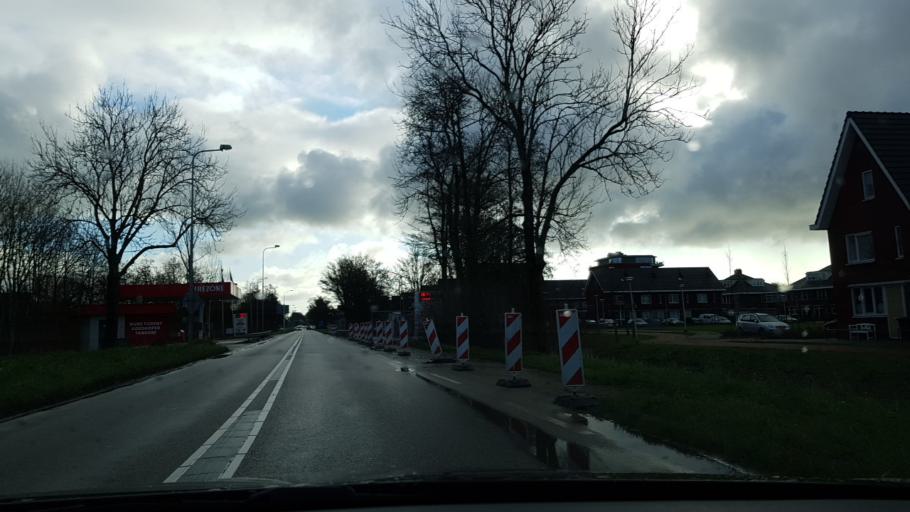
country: NL
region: North Holland
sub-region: Gemeente Uithoorn
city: Uithoorn
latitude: 52.2452
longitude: 4.8091
